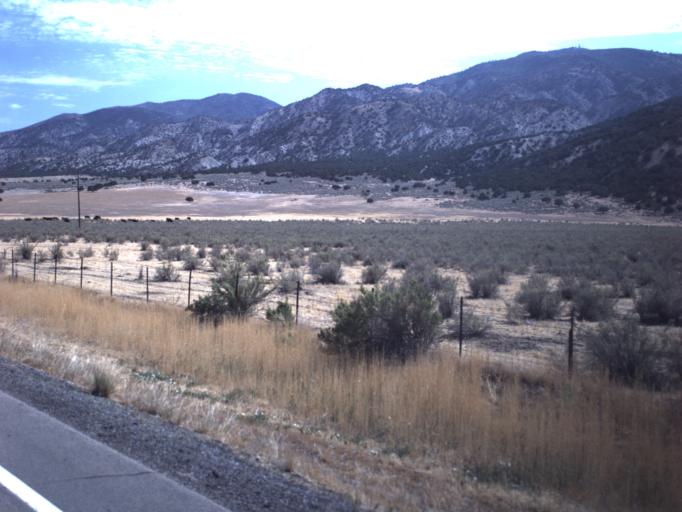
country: US
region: Utah
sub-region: Juab County
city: Nephi
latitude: 39.4834
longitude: -111.8875
